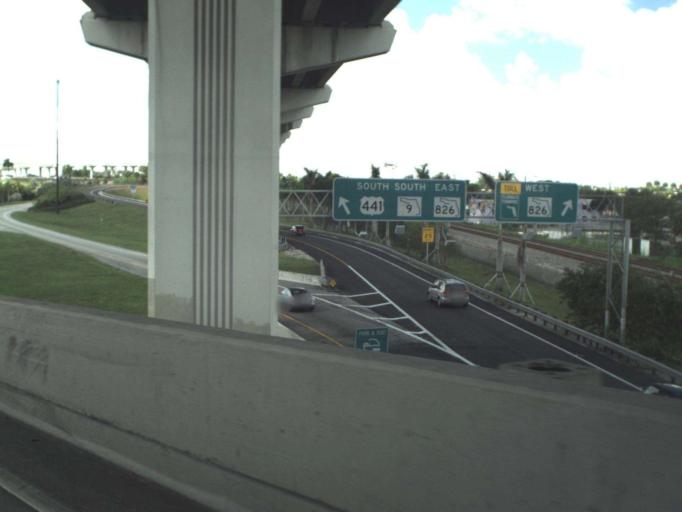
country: US
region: Florida
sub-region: Miami-Dade County
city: Norland
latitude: 25.9308
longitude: -80.2053
